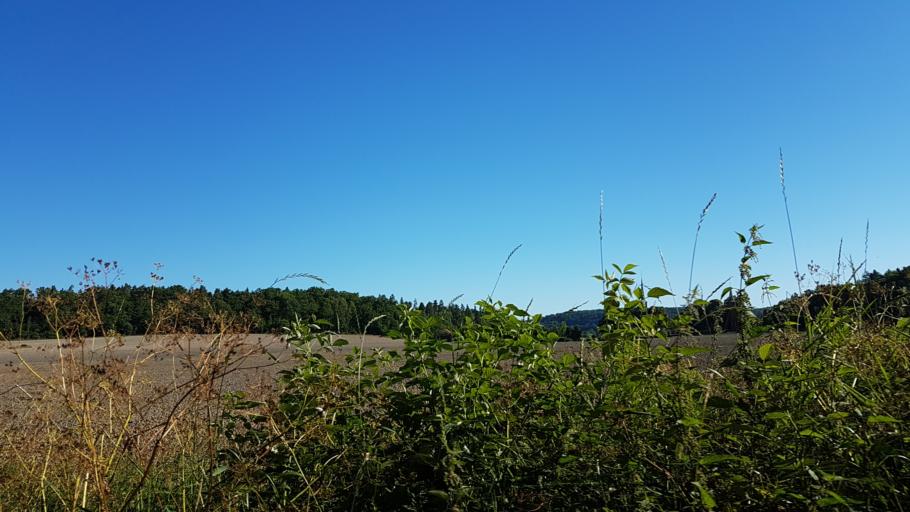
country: SE
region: OEstergoetland
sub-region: Valdemarsviks Kommun
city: Gusum
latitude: 58.4283
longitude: 16.5848
